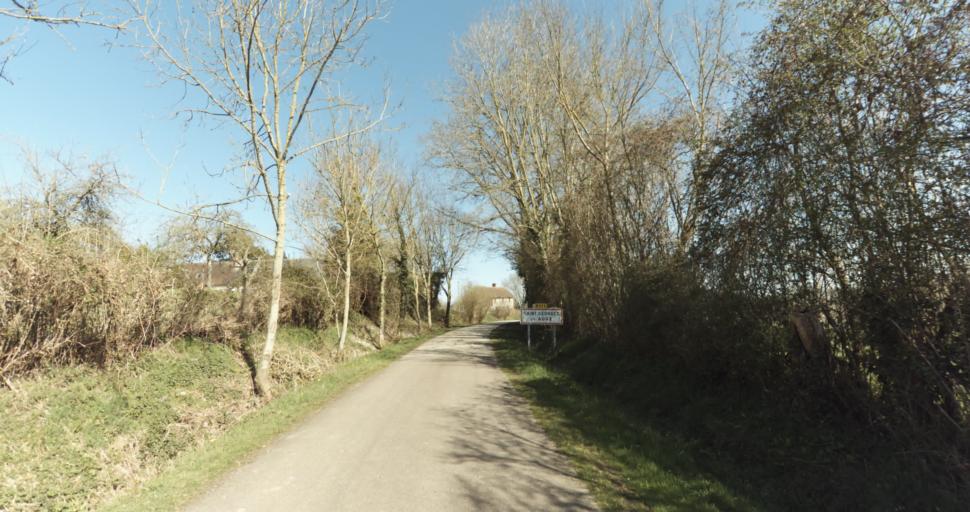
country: FR
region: Lower Normandy
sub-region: Departement du Calvados
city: Livarot
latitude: 48.9895
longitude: 0.0602
